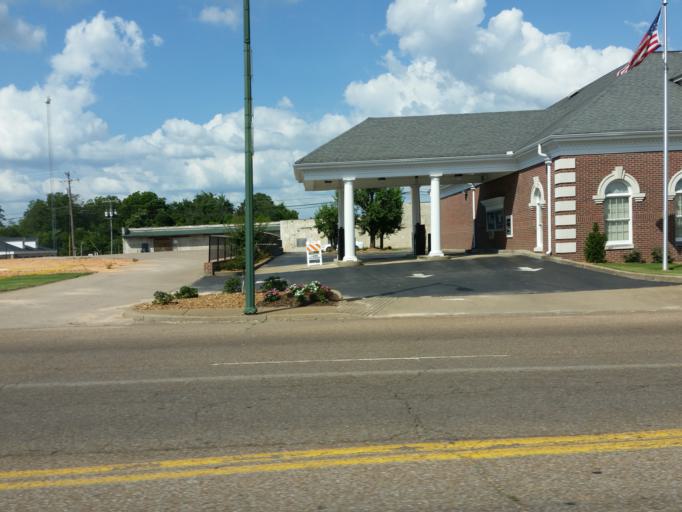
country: US
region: Tennessee
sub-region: Henderson County
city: Lexington
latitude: 35.6498
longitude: -88.3924
